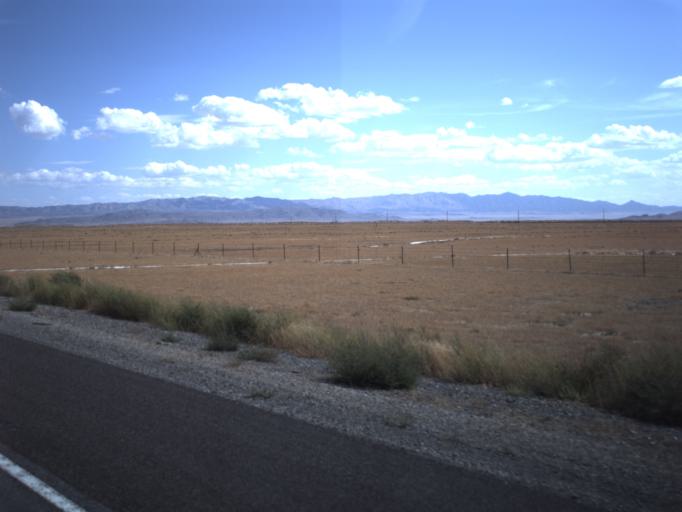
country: US
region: Utah
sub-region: Tooele County
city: Grantsville
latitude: 40.7260
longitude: -113.2199
